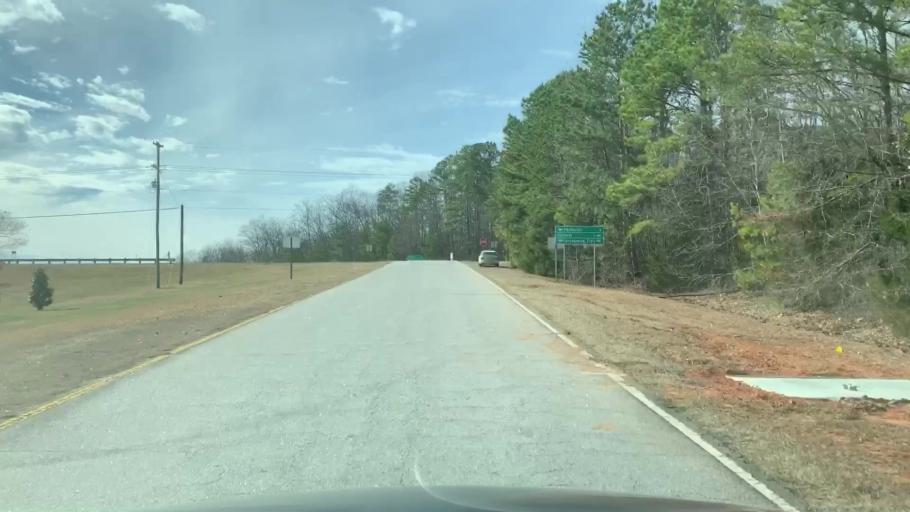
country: US
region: South Carolina
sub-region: Pickens County
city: Central
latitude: 34.6890
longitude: -82.7873
